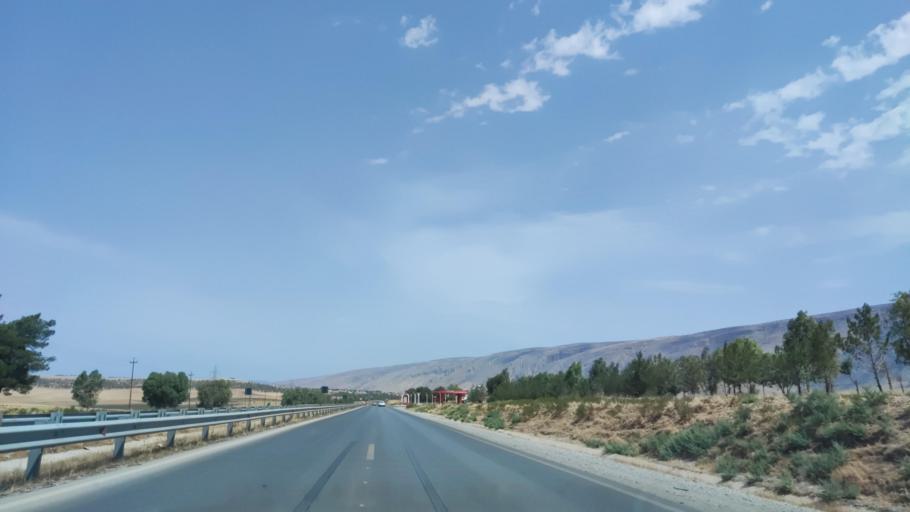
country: IQ
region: Arbil
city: Shaqlawah
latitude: 36.4674
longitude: 44.3825
